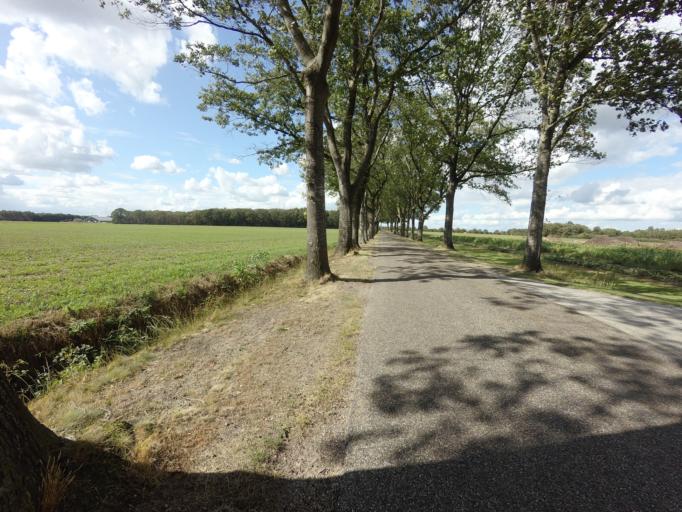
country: NL
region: Friesland
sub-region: Gemeente Heerenveen
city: Jubbega
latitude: 52.9597
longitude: 6.2061
